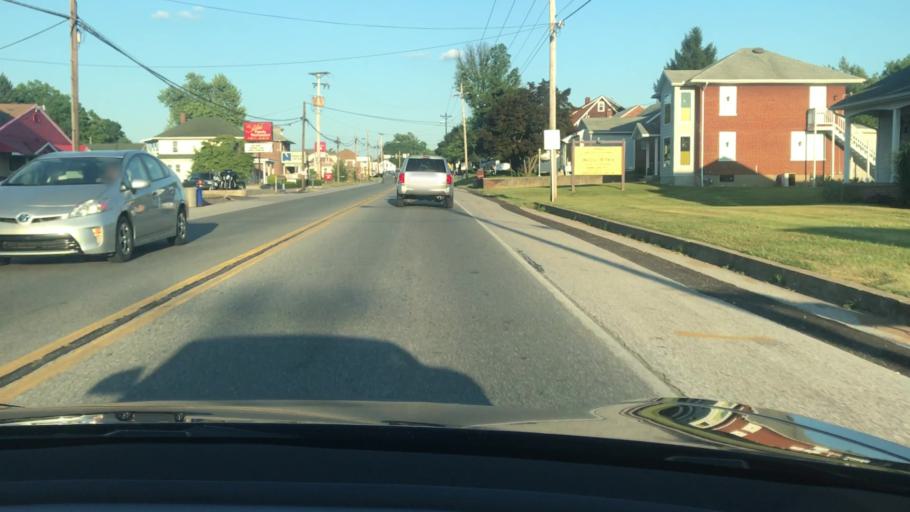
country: US
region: Pennsylvania
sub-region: York County
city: Shiloh
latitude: 39.9771
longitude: -76.7945
